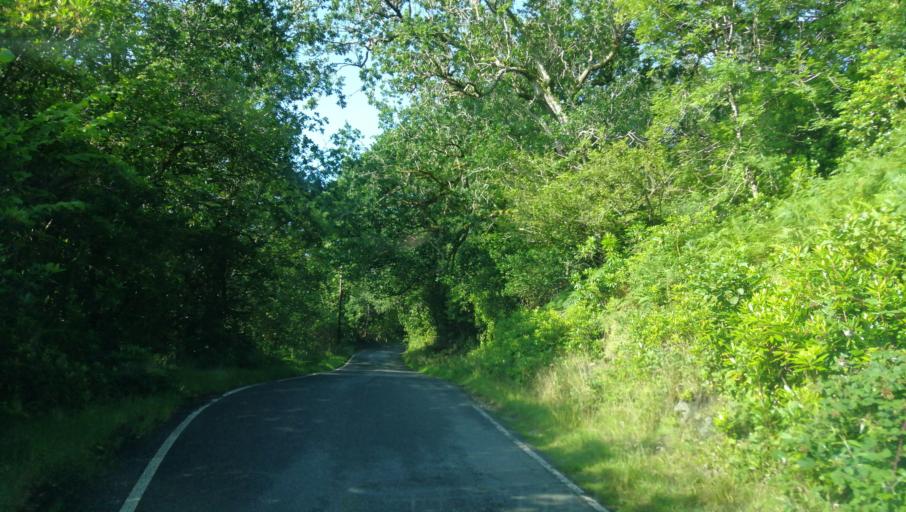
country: GB
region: Scotland
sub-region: Argyll and Bute
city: Isle Of Mull
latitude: 56.6841
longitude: -5.8237
